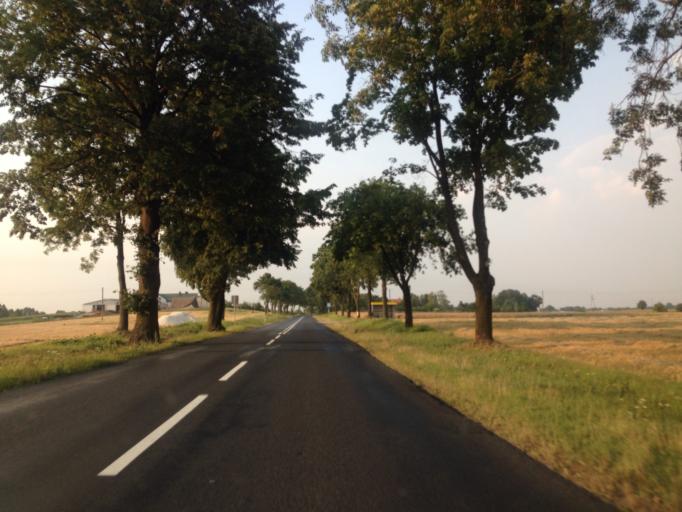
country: PL
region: Kujawsko-Pomorskie
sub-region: Powiat lipnowski
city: Chrostkowo
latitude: 52.9225
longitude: 19.2443
